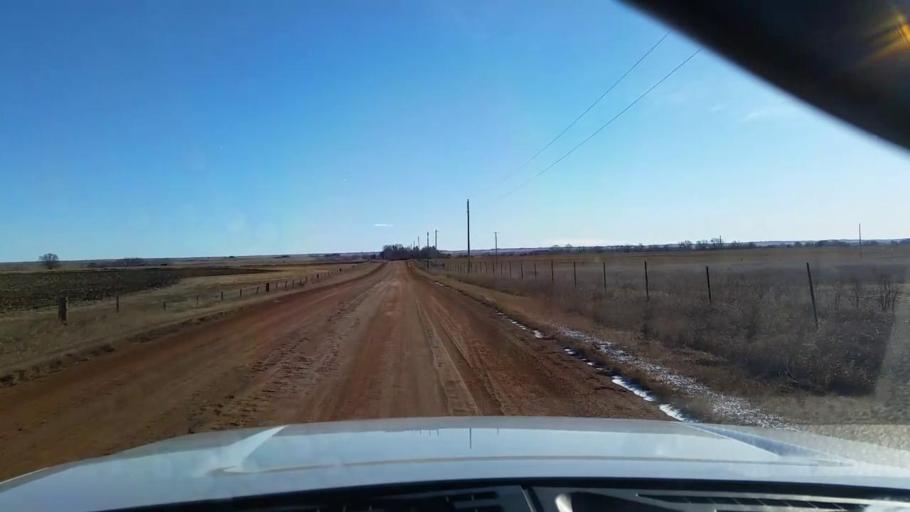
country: US
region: Colorado
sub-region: Larimer County
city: Wellington
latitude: 40.7693
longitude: -105.0624
